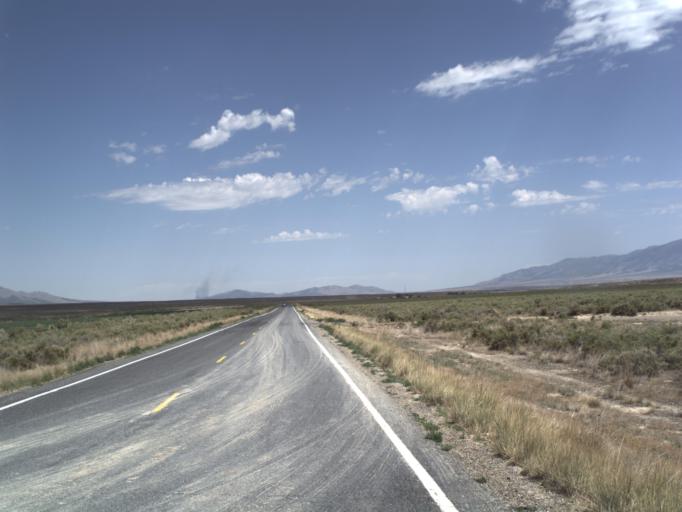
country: US
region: Utah
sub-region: Tooele County
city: Tooele
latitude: 40.1413
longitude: -112.4308
